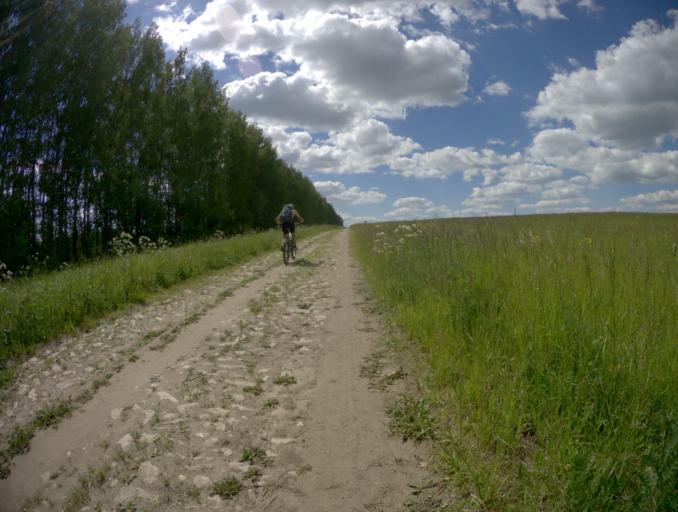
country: RU
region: Vladimir
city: Vladimir
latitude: 56.2710
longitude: 40.4137
